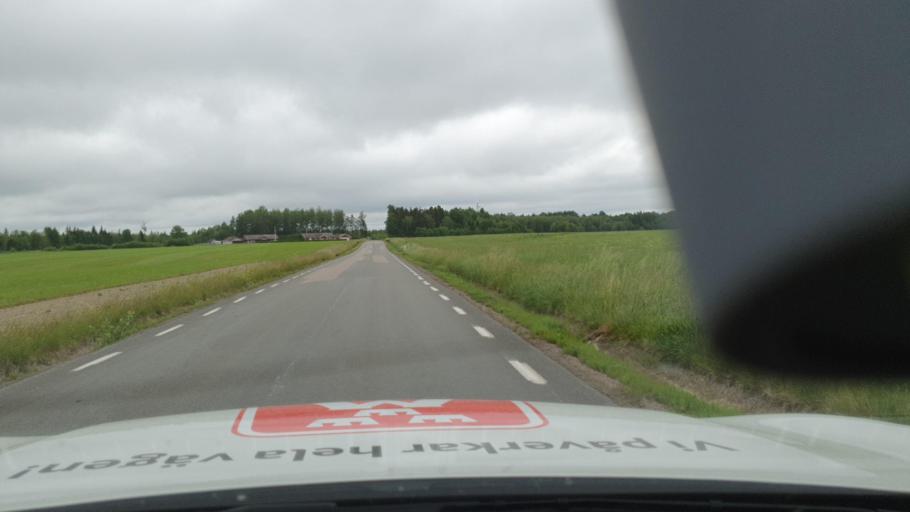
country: SE
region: Vaestra Goetaland
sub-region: Tibro Kommun
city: Tibro
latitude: 58.3833
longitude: 14.0557
